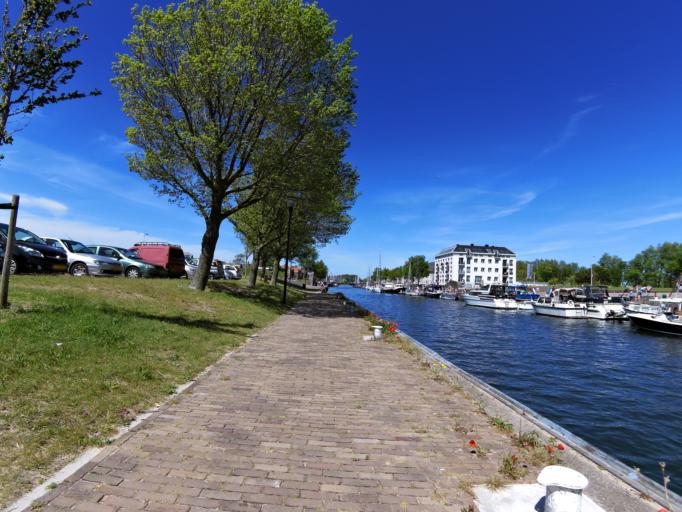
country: NL
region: South Holland
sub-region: Gemeente Hellevoetsluis
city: Hellevoetsluis
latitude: 51.8202
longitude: 4.1280
